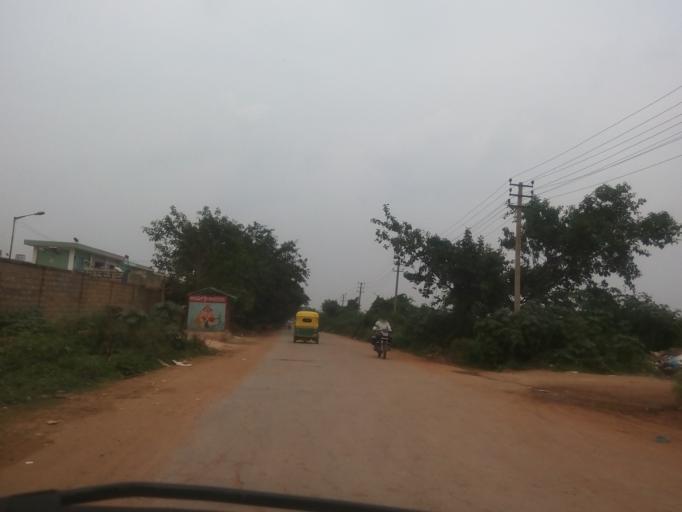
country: IN
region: Karnataka
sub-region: Bangalore Urban
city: Anekal
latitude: 12.8423
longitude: 77.6876
